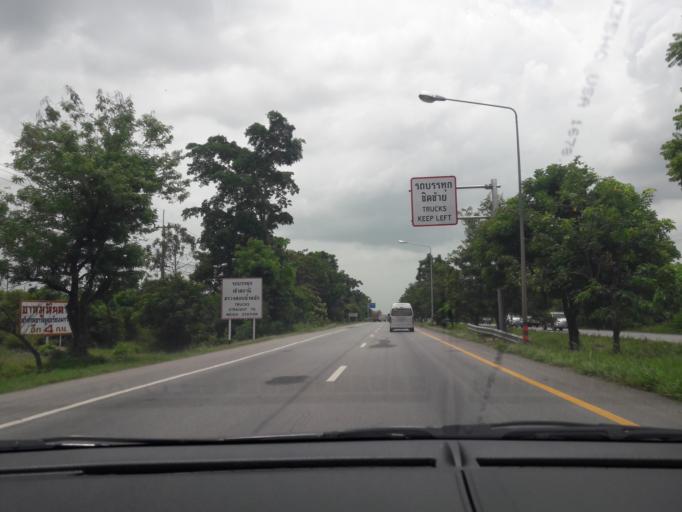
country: TH
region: Nakhon Ratchasima
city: Chaloem Phra Kiat
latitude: 15.0864
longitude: 102.2370
